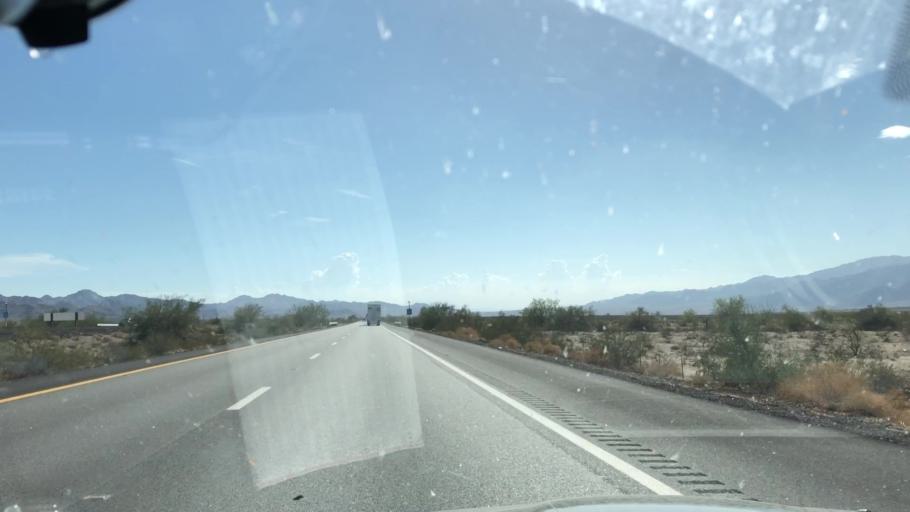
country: US
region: California
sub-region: Imperial County
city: Niland
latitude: 33.6815
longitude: -115.5471
